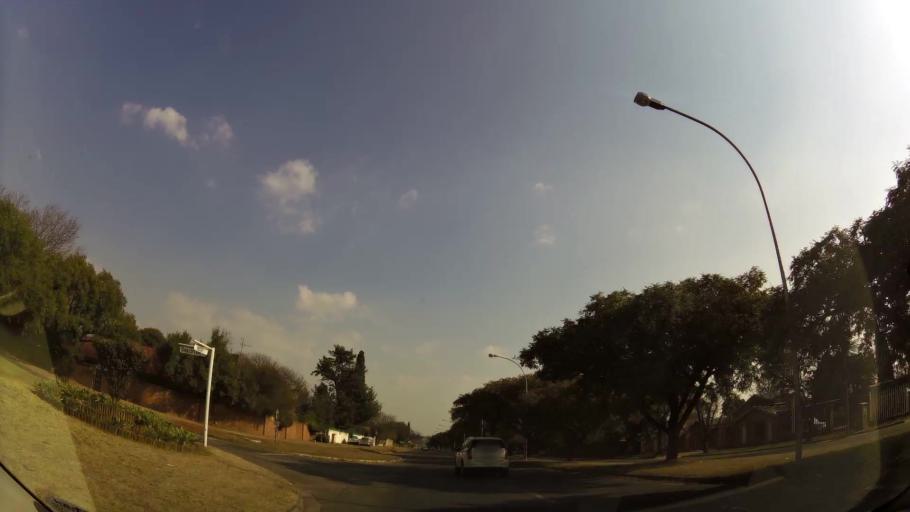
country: ZA
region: Gauteng
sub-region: Ekurhuleni Metropolitan Municipality
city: Benoni
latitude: -26.1537
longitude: 28.2938
